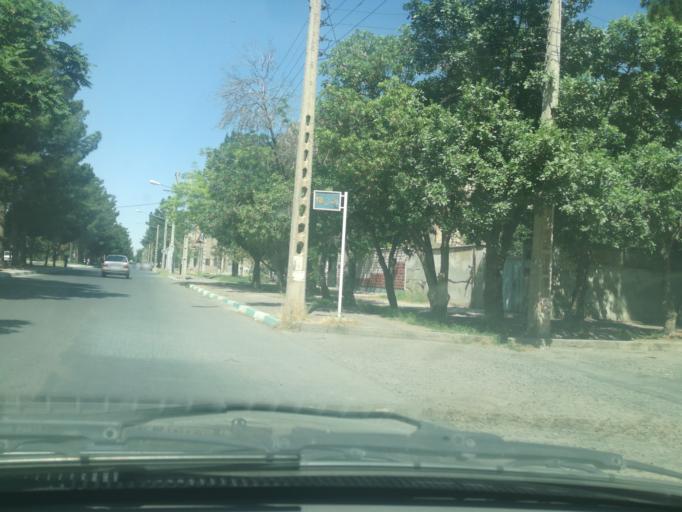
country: IR
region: Razavi Khorasan
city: Sarakhs
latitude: 36.5377
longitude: 61.1536
